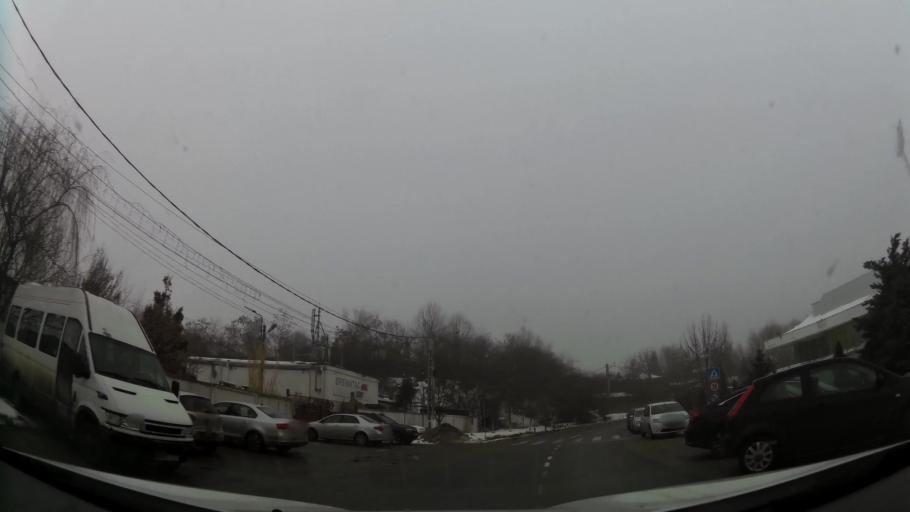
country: RO
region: Ilfov
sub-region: Comuna Chiajna
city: Chiajna
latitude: 44.4635
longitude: 25.9768
